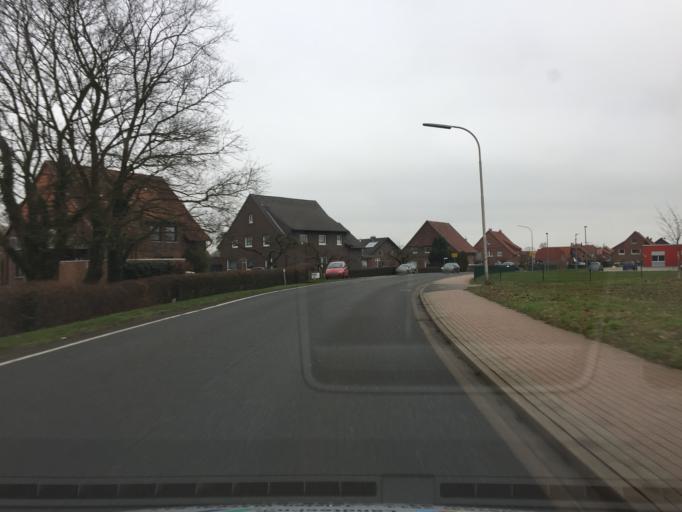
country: DE
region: Lower Saxony
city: Niedernwohren
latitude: 52.3450
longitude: 9.1405
